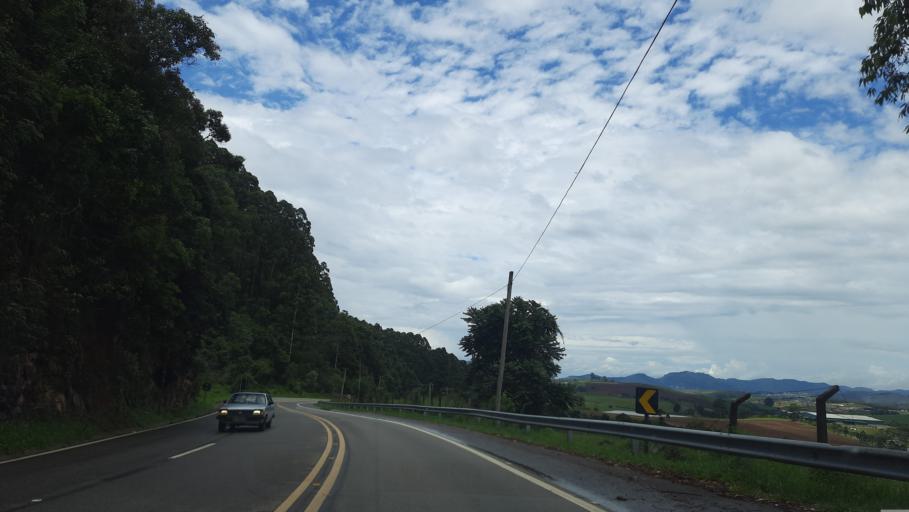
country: BR
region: Minas Gerais
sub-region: Pocos De Caldas
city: Pocos de Caldas
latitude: -21.8466
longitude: -46.6890
